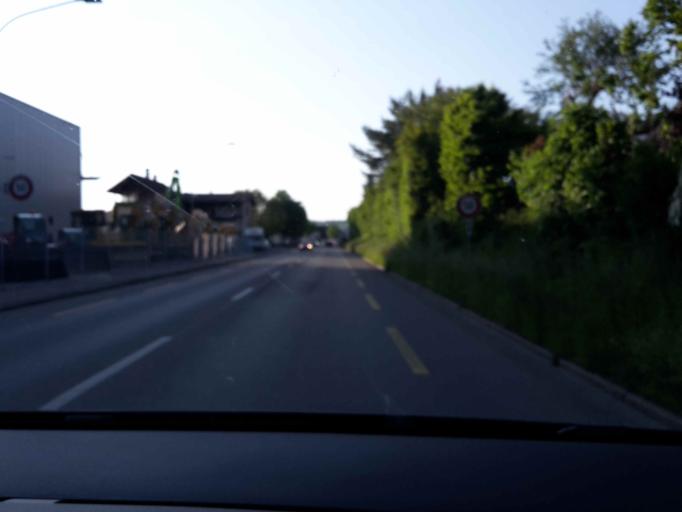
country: CH
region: Bern
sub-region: Thun District
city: Steffisburg
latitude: 46.7774
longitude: 7.6139
